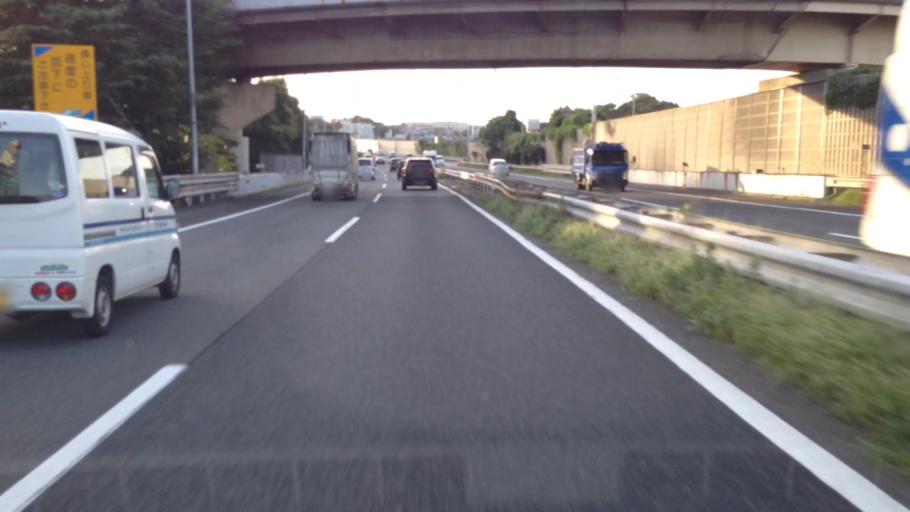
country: JP
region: Kanagawa
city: Kamakura
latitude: 35.3822
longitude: 139.5845
